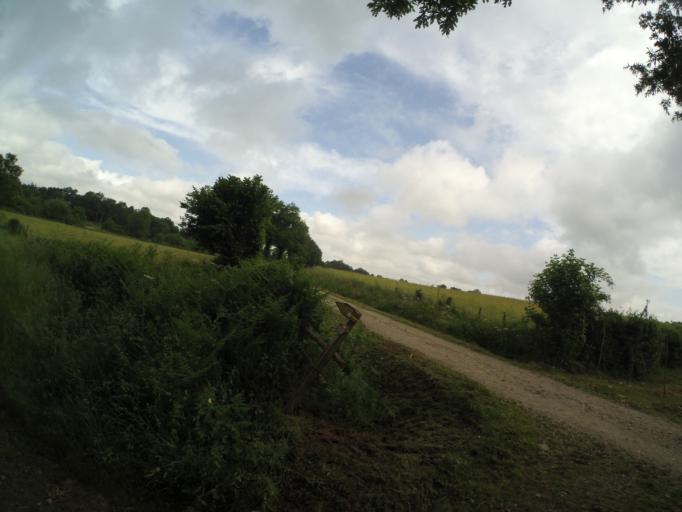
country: FR
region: Pays de la Loire
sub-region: Departement de la Vendee
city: Nesmy
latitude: 46.6115
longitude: -1.3967
